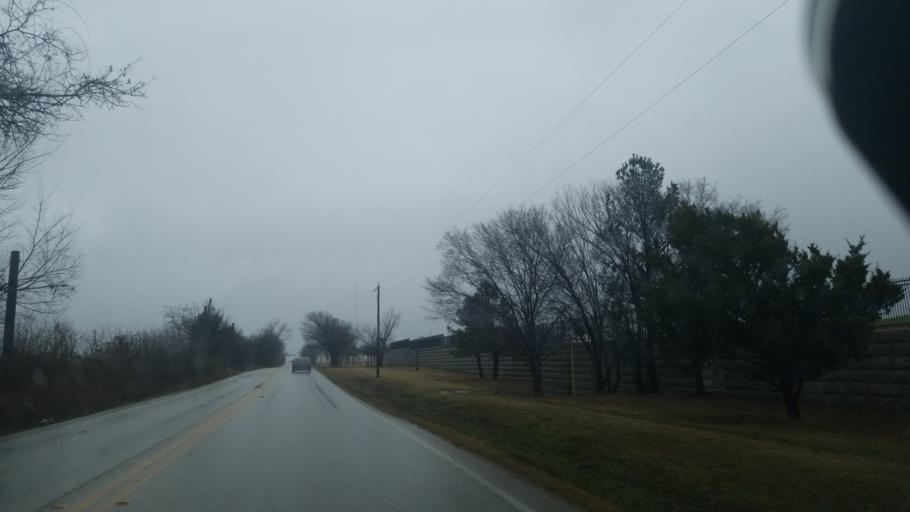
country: US
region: Texas
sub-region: Denton County
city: Corinth
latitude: 33.1901
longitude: -97.0852
